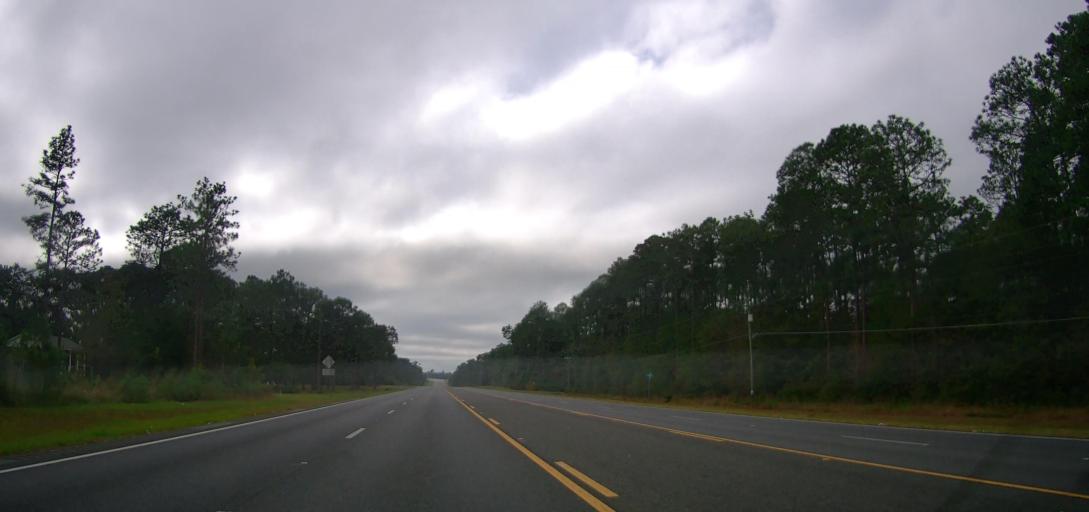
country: US
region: Georgia
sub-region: Colquitt County
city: Moultrie
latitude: 31.0896
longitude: -83.8086
